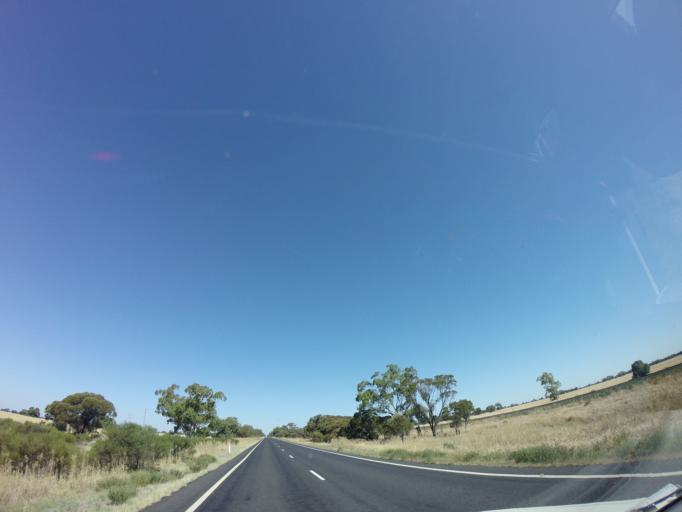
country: AU
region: New South Wales
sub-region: Bogan
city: Nyngan
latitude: -31.7892
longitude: 147.6256
